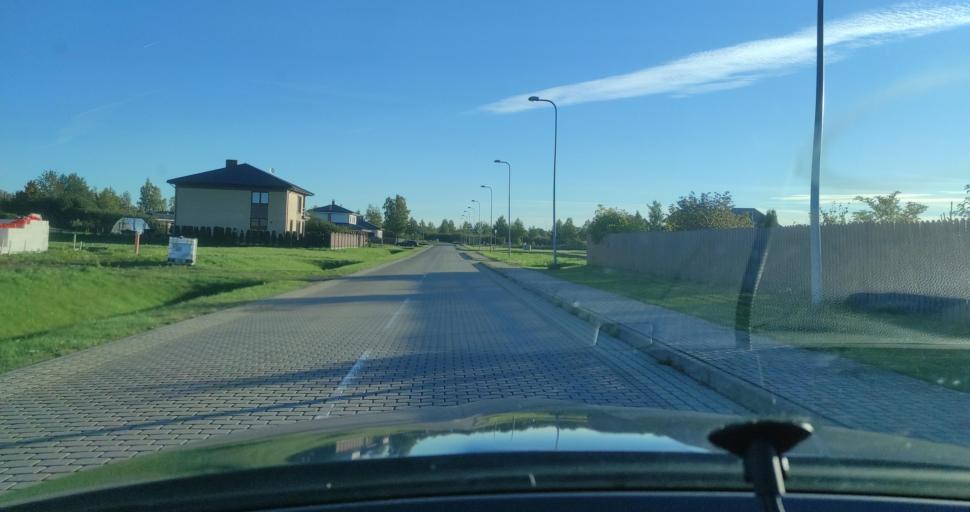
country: LV
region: Ventspils
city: Ventspils
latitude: 57.3675
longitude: 21.5741
